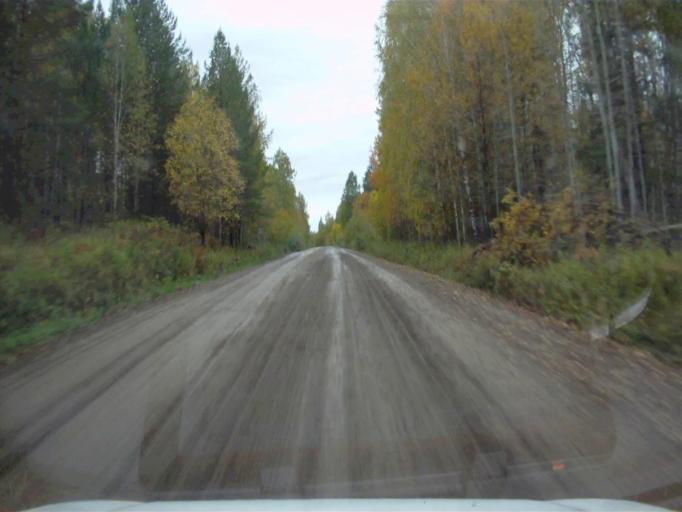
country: RU
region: Chelyabinsk
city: Nyazepetrovsk
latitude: 56.1065
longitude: 59.3820
